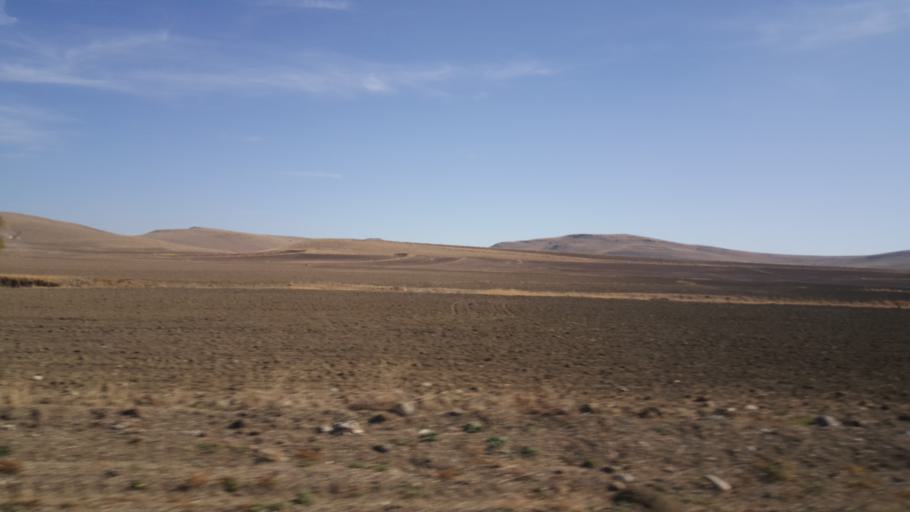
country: TR
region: Ankara
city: Yenice
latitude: 39.3566
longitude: 32.7949
